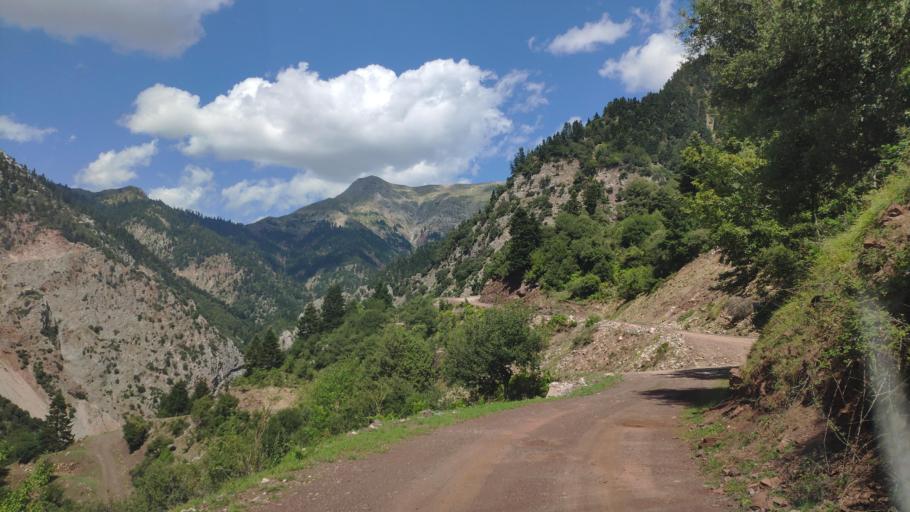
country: GR
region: Central Greece
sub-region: Nomos Evrytanias
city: Kerasochori
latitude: 39.1346
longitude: 21.6566
